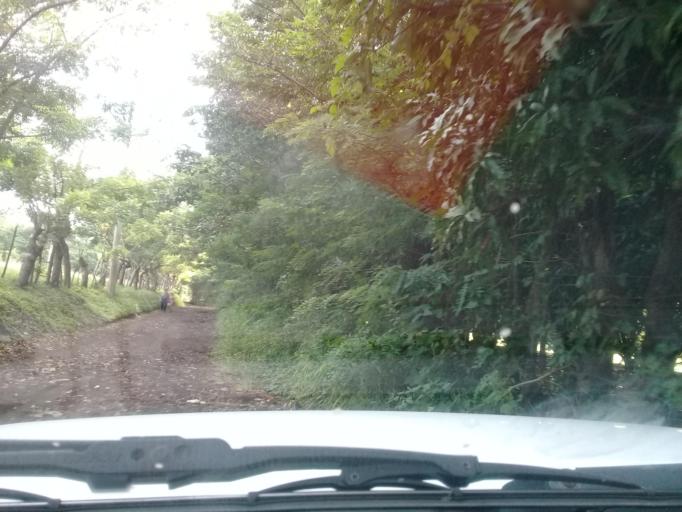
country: MX
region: Veracruz
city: Catemaco
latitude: 18.4376
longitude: -95.1309
